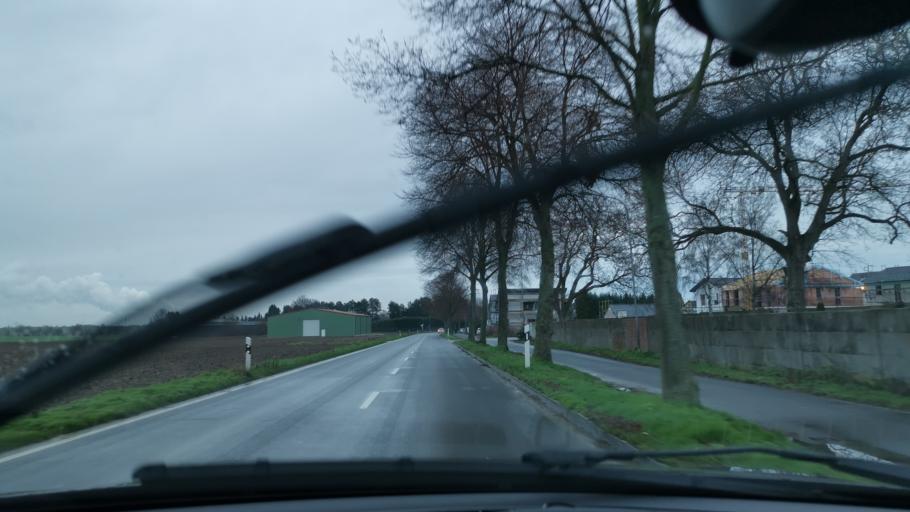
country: DE
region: North Rhine-Westphalia
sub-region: Regierungsbezirk Koln
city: Bedburg
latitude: 50.9846
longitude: 6.5187
